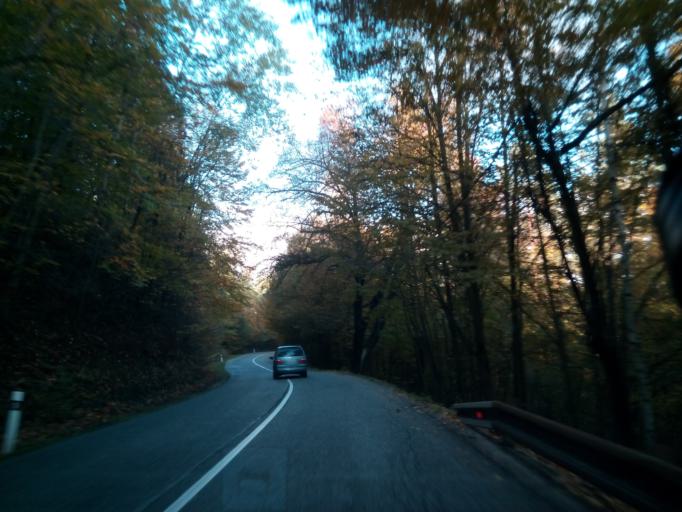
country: SK
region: Kosicky
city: Gelnica
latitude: 48.9089
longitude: 20.9611
